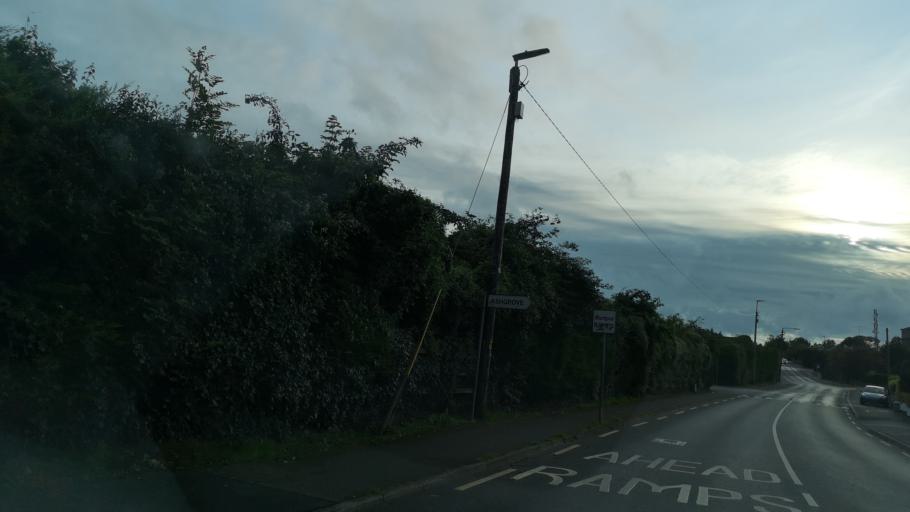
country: IE
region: Leinster
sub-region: An Iarmhi
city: Athlone
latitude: 53.4220
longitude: -7.9058
